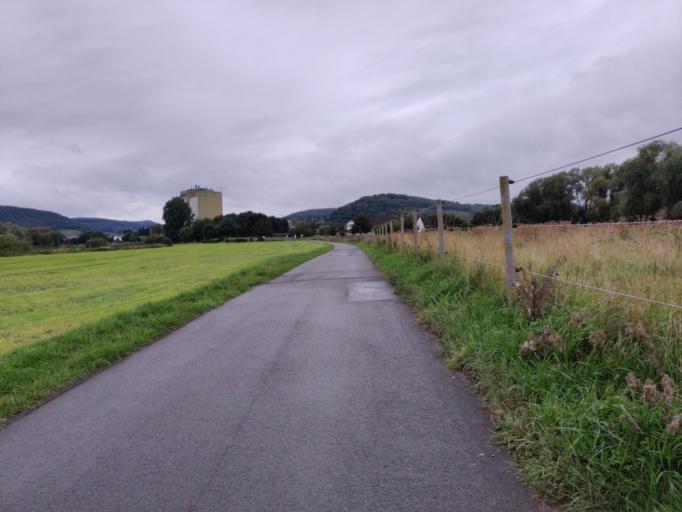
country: DE
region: North Rhine-Westphalia
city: Beverungen
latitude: 51.6719
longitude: 9.3869
